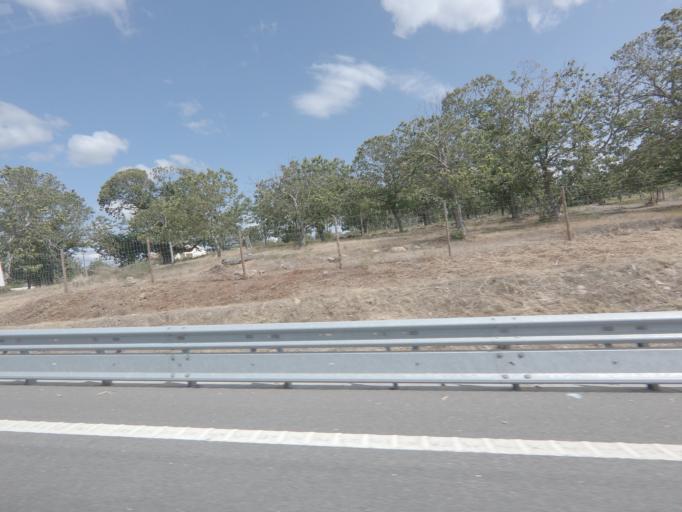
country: PT
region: Vila Real
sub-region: Santa Marta de Penaguiao
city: Santa Marta de Penaguiao
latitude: 41.2697
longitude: -7.8165
